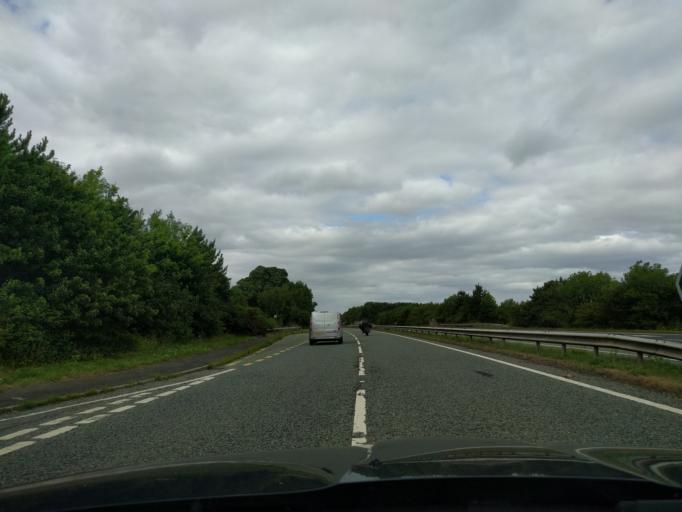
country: GB
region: England
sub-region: Northumberland
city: Ellingham
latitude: 55.5007
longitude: -1.7333
